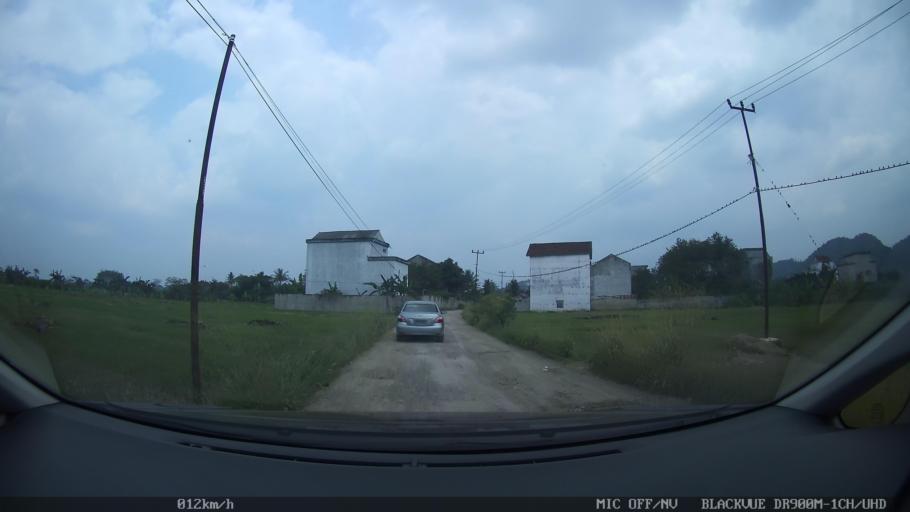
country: ID
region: Lampung
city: Gadingrejo
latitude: -5.3739
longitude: 105.0294
